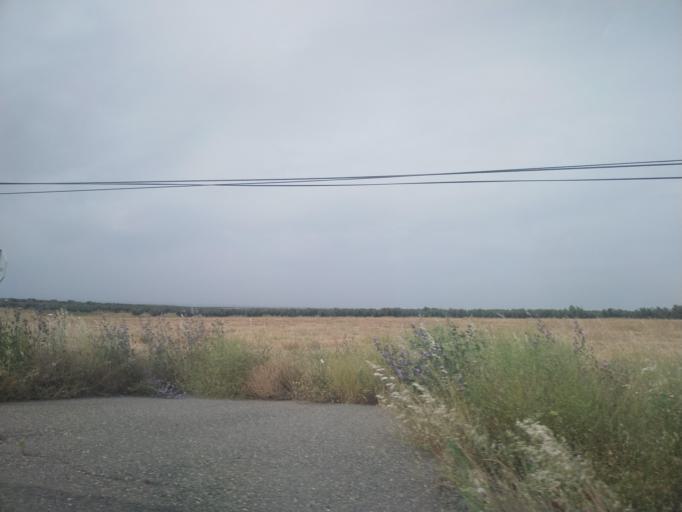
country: ES
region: Castille-La Mancha
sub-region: Province of Toledo
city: Casasbuenas
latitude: 39.7661
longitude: -4.1395
